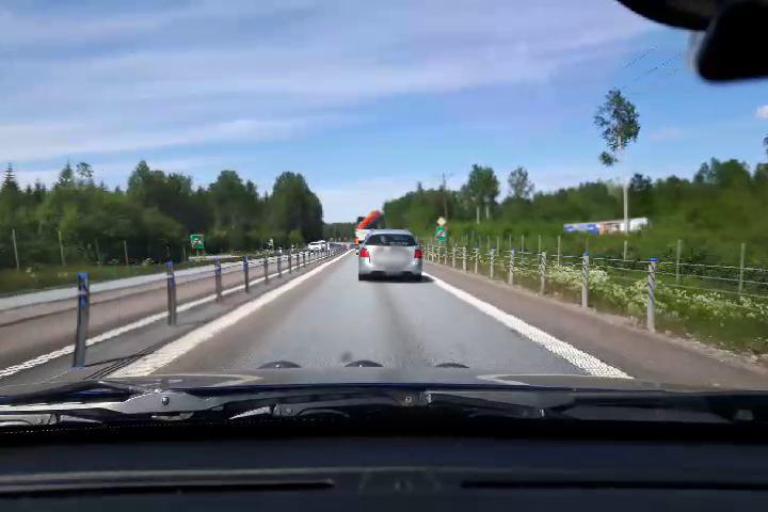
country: SE
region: Gaevleborg
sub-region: Gavle Kommun
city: Norrsundet
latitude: 60.9548
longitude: 17.0337
